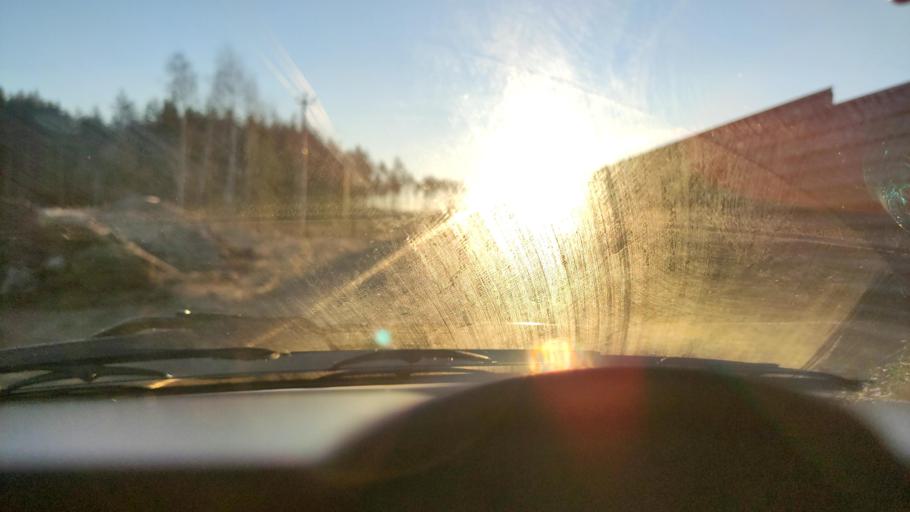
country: RU
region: Voronezj
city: Podgornoye
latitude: 51.7504
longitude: 39.1405
